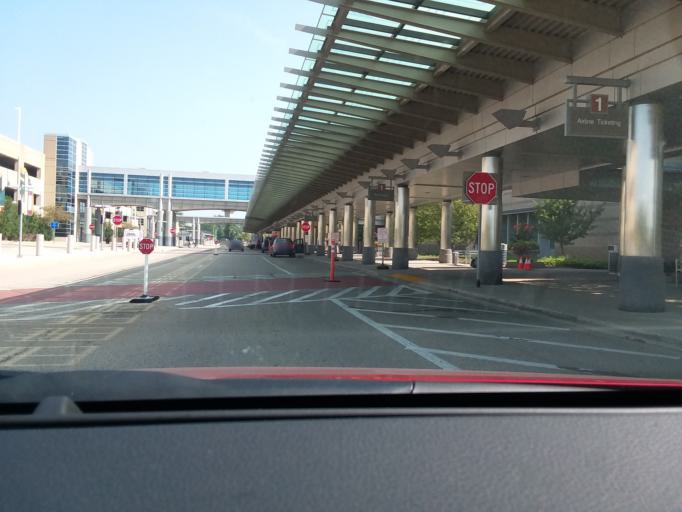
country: US
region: Wisconsin
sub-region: Dane County
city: Maple Bluff
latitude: 43.1352
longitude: -89.3465
